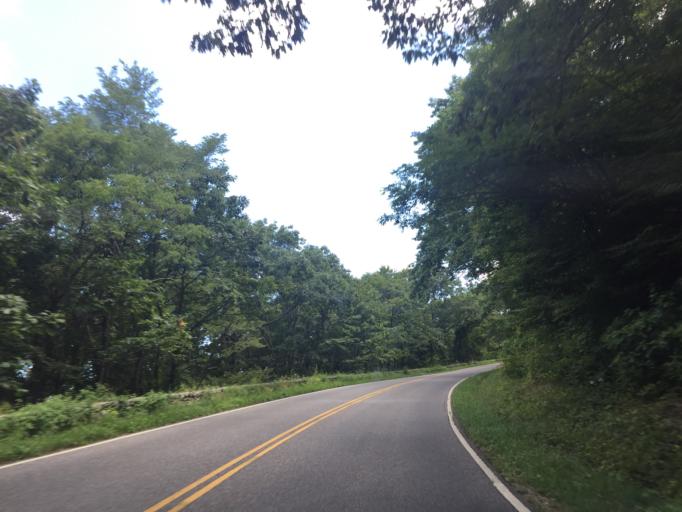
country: US
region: Virginia
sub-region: Page County
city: Luray
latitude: 38.6290
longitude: -78.3220
